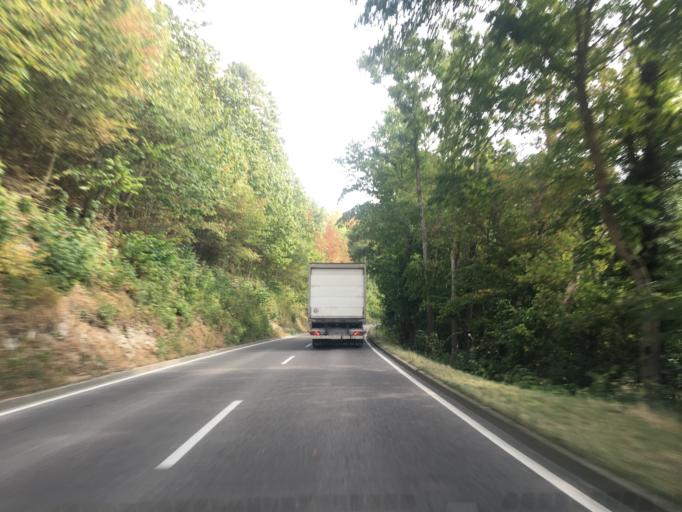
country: DE
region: Baden-Wuerttemberg
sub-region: Tuebingen Region
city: Pfullingen
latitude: 48.4201
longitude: 9.1802
